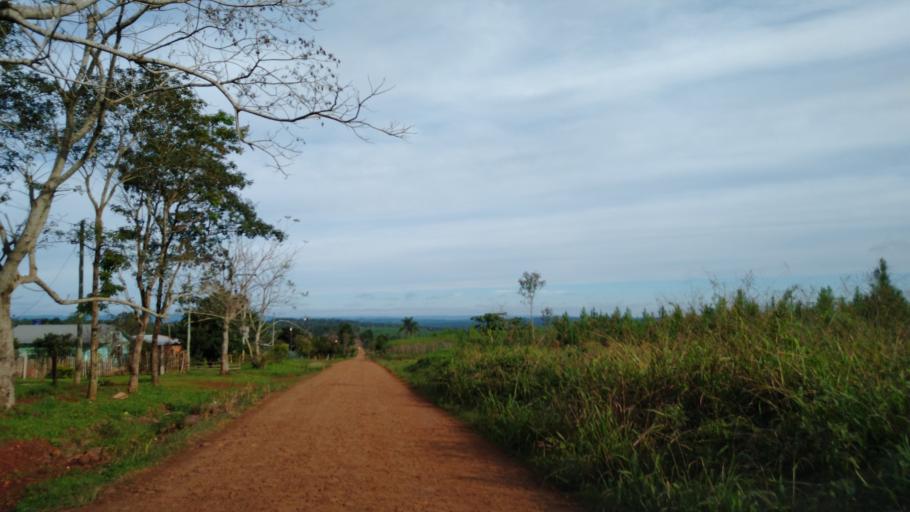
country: AR
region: Misiones
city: Capiovi
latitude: -26.9458
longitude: -55.0965
